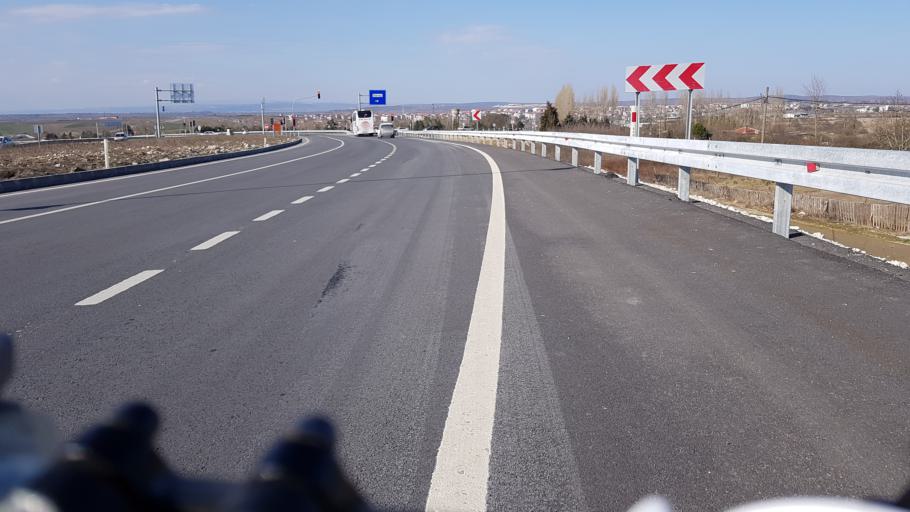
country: TR
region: Tekirdag
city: Saray
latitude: 41.4168
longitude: 27.9222
